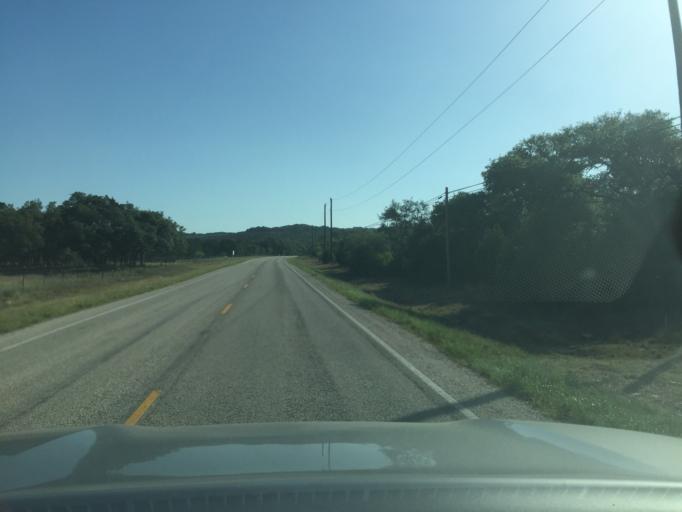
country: US
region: Texas
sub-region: Blanco County
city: Blanco
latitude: 30.1223
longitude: -98.2987
